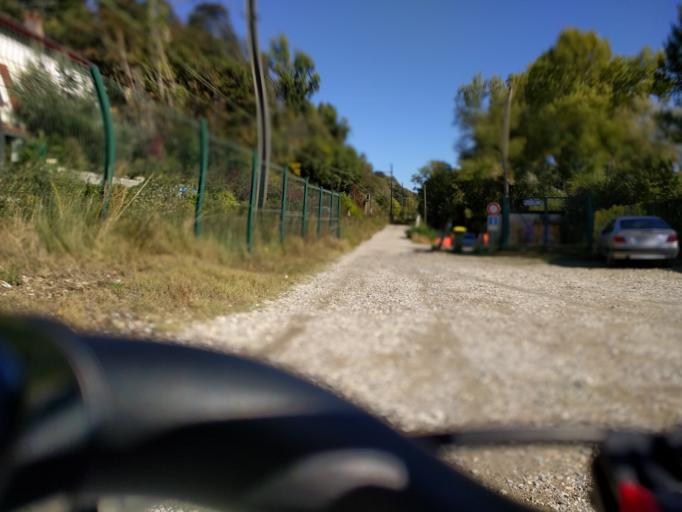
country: FR
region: Rhone-Alpes
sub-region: Departement du Rhone
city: Sathonay-Camp
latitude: 45.7963
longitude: 4.8775
